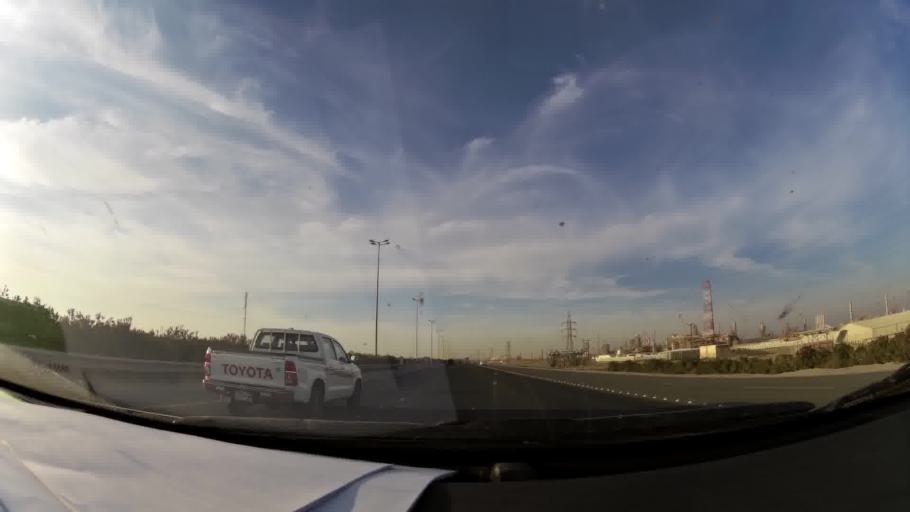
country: KW
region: Al Ahmadi
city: Al Fahahil
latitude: 28.9860
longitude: 48.1512
